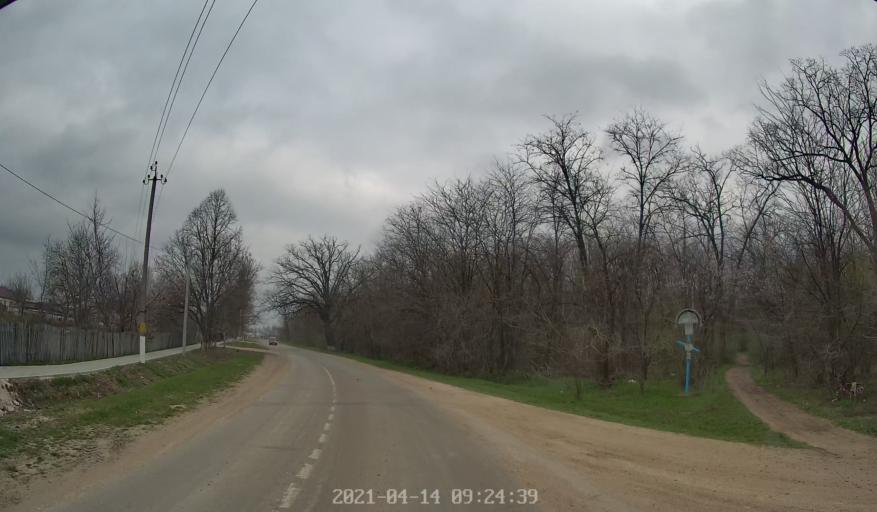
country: MD
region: Chisinau
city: Vadul lui Voda
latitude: 47.1107
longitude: 29.1142
